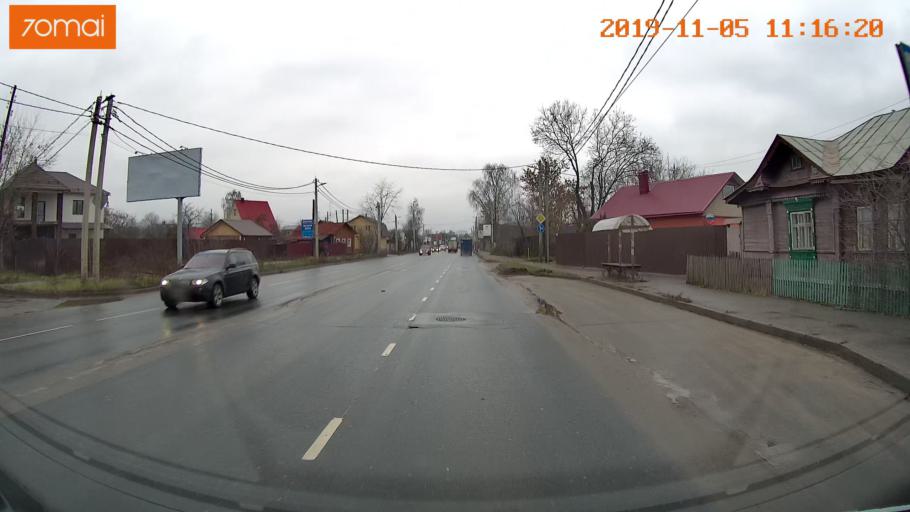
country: RU
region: Ivanovo
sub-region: Gorod Ivanovo
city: Ivanovo
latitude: 56.9840
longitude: 40.9535
